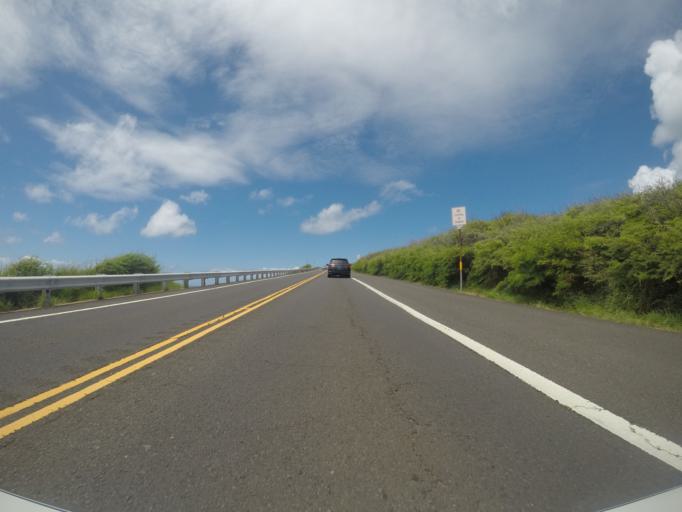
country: US
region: Hawaii
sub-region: Honolulu County
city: Waimanalo Beach
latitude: 21.2748
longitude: -157.6881
